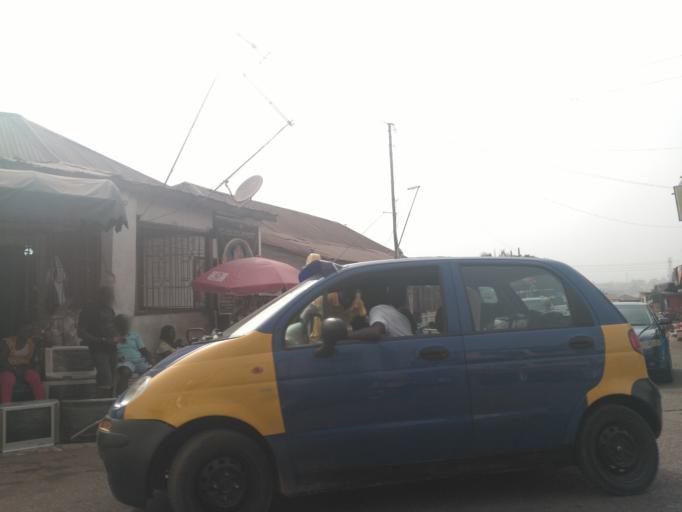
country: GH
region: Ashanti
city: Kumasi
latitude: 6.7007
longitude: -1.6321
